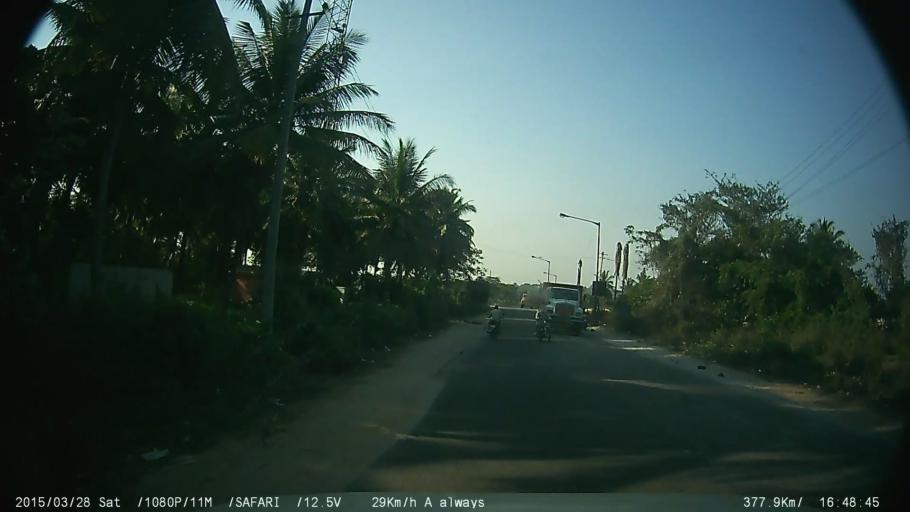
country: IN
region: Karnataka
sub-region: Mandya
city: Shrirangapattana
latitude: 12.4173
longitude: 76.5811
